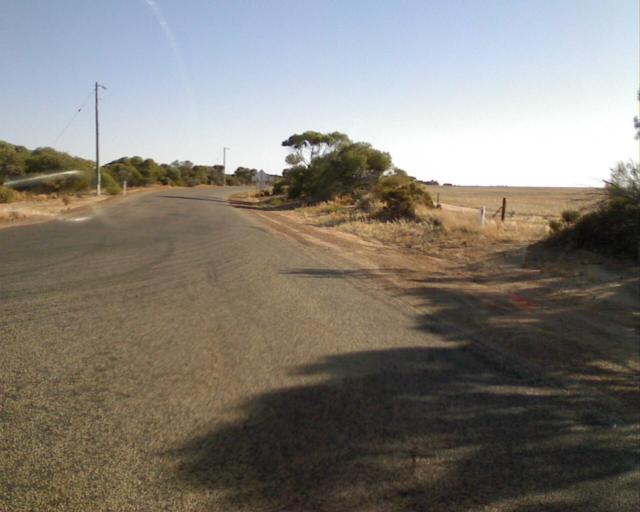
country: AU
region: Western Australia
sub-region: Wongan-Ballidu
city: Wongan Hills
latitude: -30.5226
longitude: 117.1752
